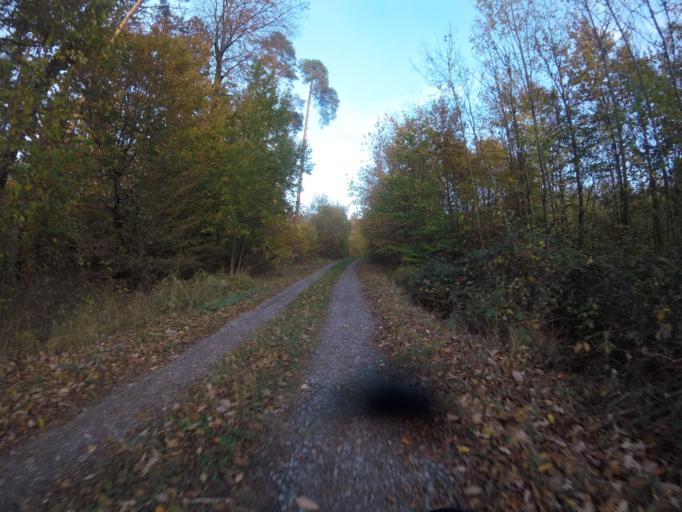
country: DE
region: Baden-Wuerttemberg
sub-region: Regierungsbezirk Stuttgart
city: Kirchberg an der Murr
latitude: 48.9821
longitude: 9.3416
